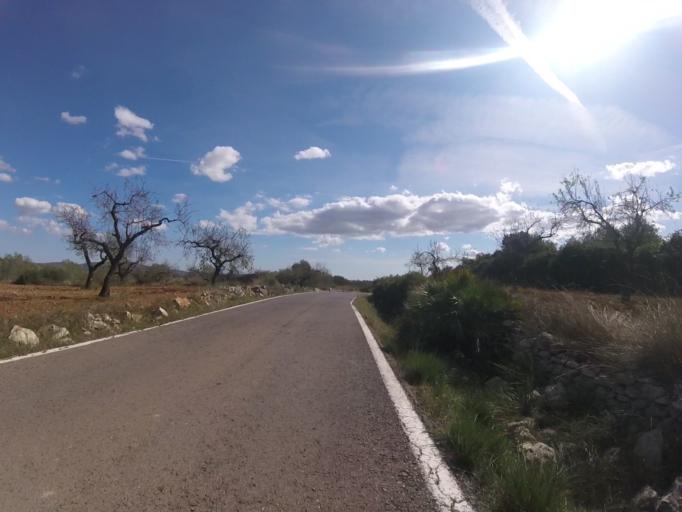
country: ES
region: Valencia
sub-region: Provincia de Castello
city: Albocasser
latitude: 40.4009
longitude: 0.0853
